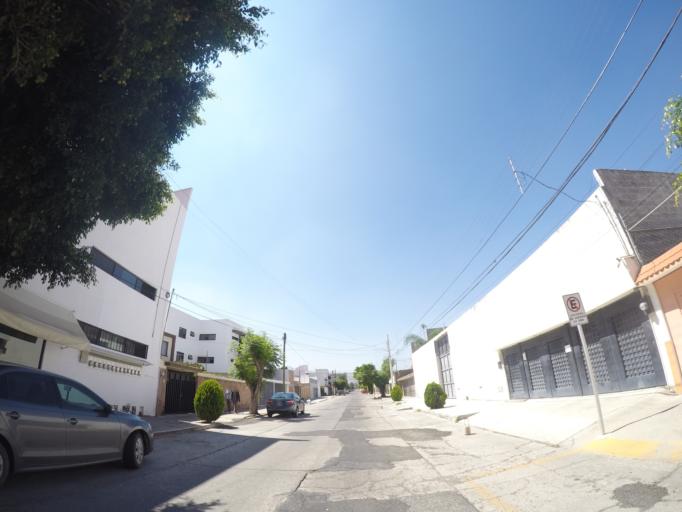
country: MX
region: San Luis Potosi
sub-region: San Luis Potosi
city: San Luis Potosi
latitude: 22.1461
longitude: -101.0099
